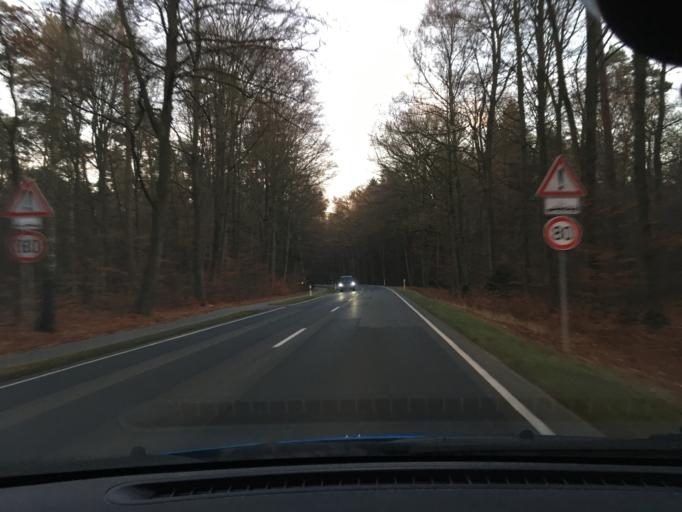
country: DE
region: Lower Saxony
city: Uelzen
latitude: 52.9839
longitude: 10.5191
